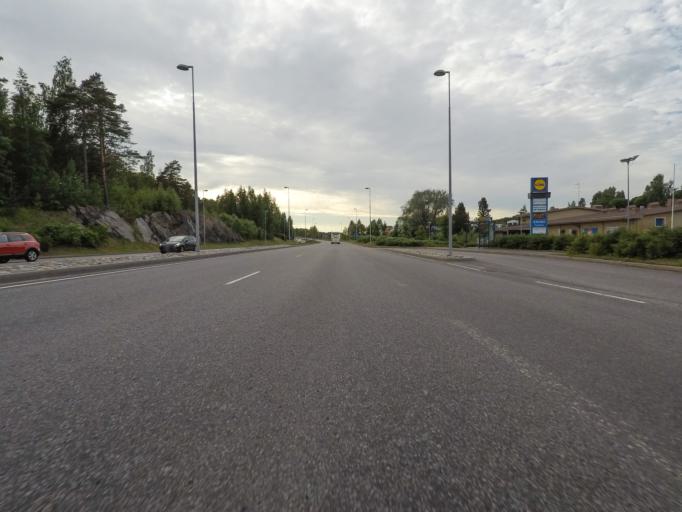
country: FI
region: Southern Savonia
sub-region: Savonlinna
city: Savonlinna
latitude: 61.8684
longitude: 28.9239
